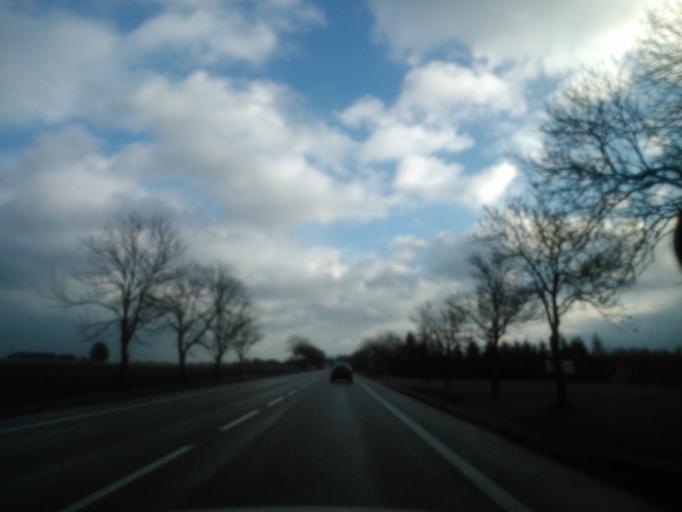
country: PL
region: Masovian Voivodeship
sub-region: Powiat sierpecki
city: Rosciszewo
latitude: 52.8280
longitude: 19.7579
